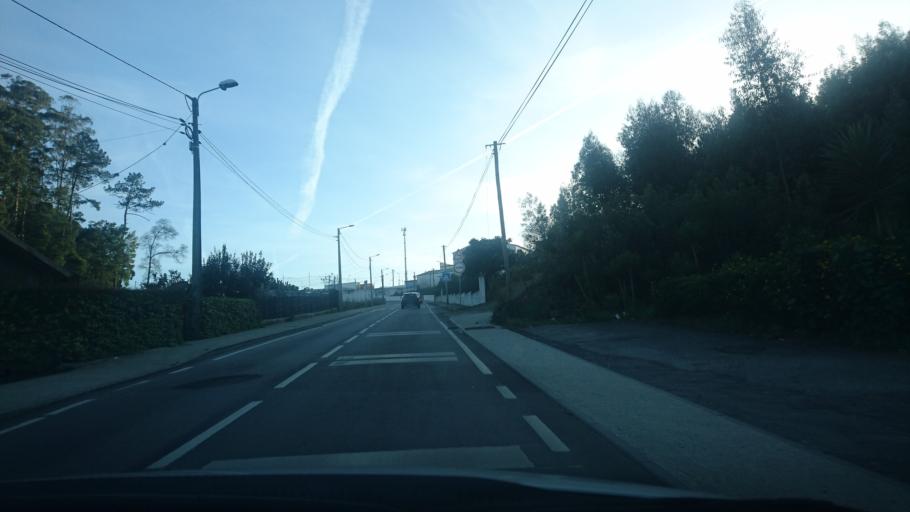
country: PT
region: Aveiro
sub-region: Espinho
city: Souto
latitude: 40.9748
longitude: -8.6072
